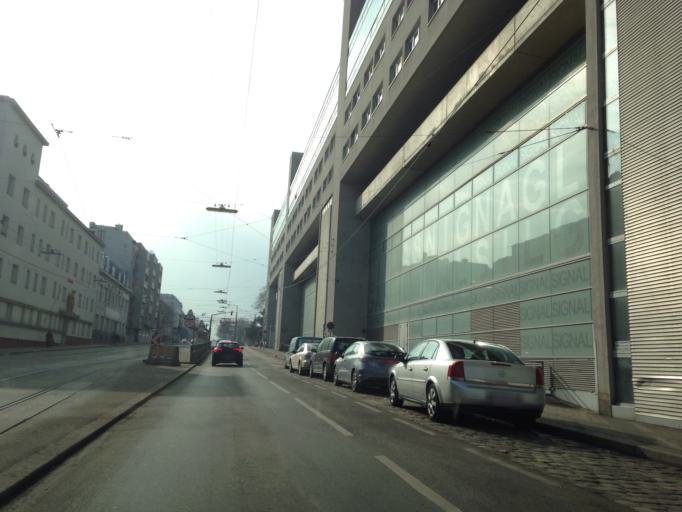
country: AT
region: Vienna
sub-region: Wien Stadt
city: Vienna
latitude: 48.2101
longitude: 16.3054
